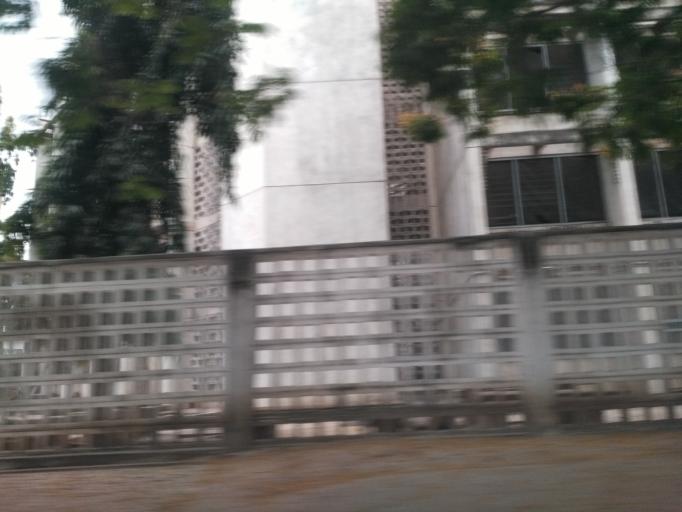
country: TZ
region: Dar es Salaam
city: Dar es Salaam
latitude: -6.8148
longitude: 39.2938
